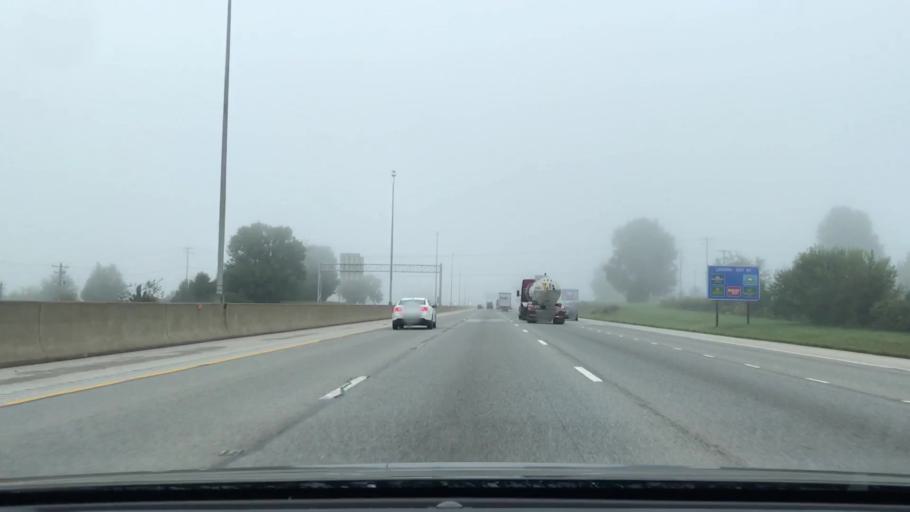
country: US
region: Kentucky
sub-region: Warren County
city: Plano
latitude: 36.9253
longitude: -86.4231
